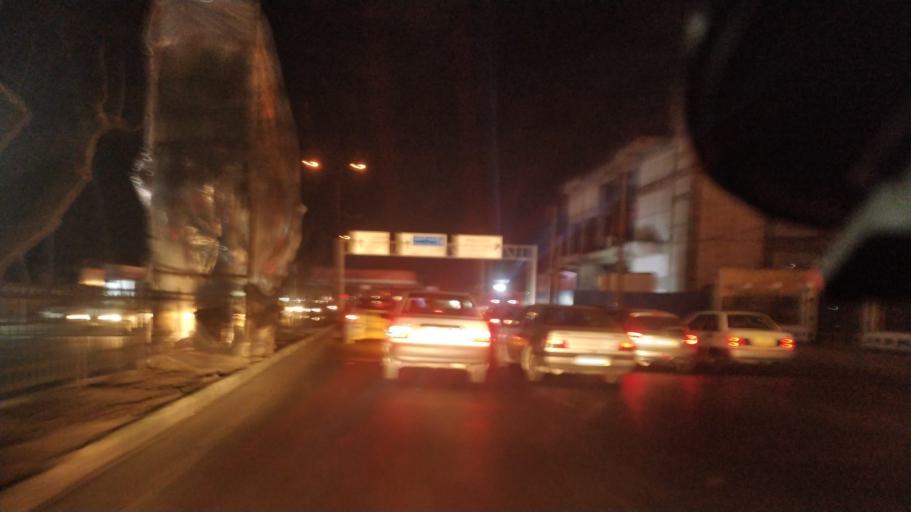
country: IR
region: Alborz
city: Karaj
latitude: 35.7809
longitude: 51.0062
